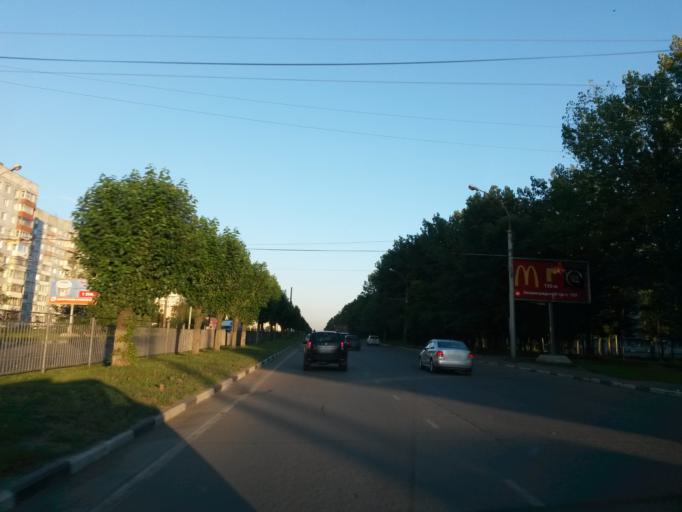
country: RU
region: Jaroslavl
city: Yaroslavl
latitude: 57.6953
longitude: 39.7682
